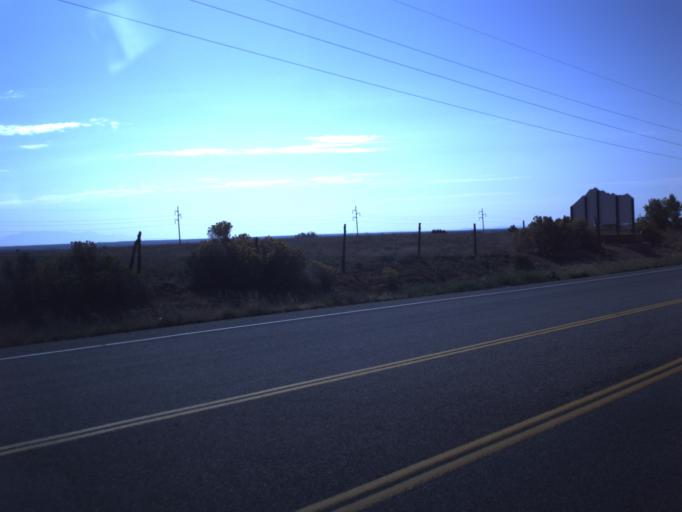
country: US
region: Utah
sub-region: San Juan County
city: Blanding
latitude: 37.5948
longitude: -109.4786
